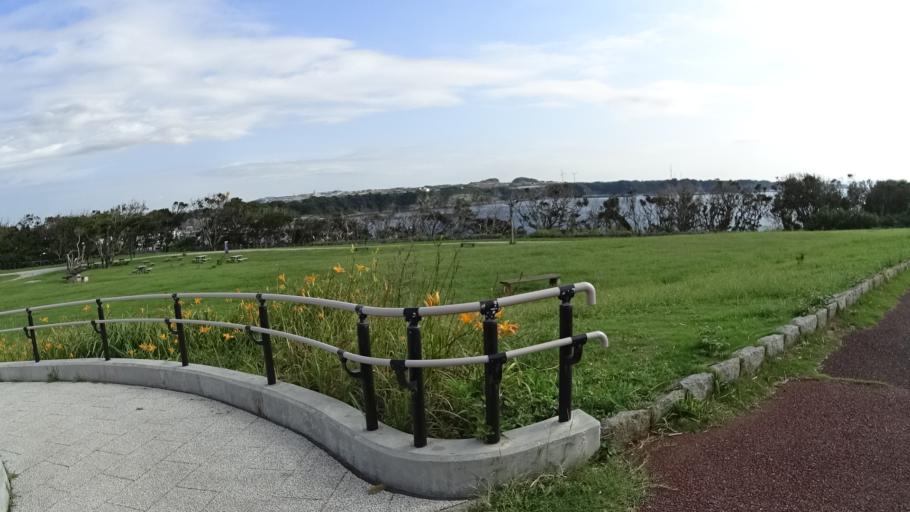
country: JP
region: Kanagawa
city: Miura
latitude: 35.1310
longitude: 139.6254
